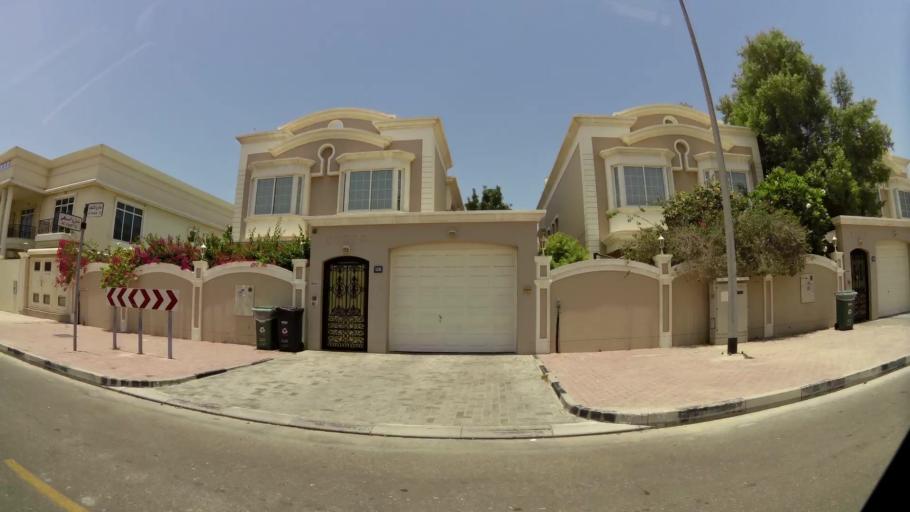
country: AE
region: Dubai
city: Dubai
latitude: 25.1777
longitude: 55.2242
